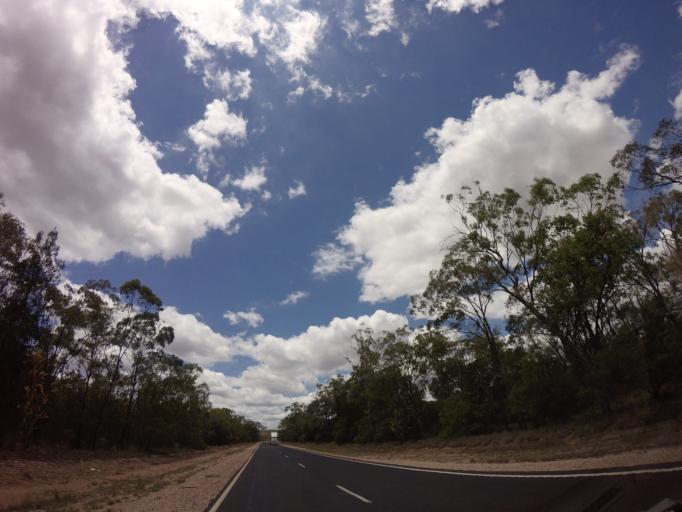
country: AU
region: Queensland
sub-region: Goondiwindi
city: Goondiwindi
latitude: -28.0406
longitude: 150.7989
